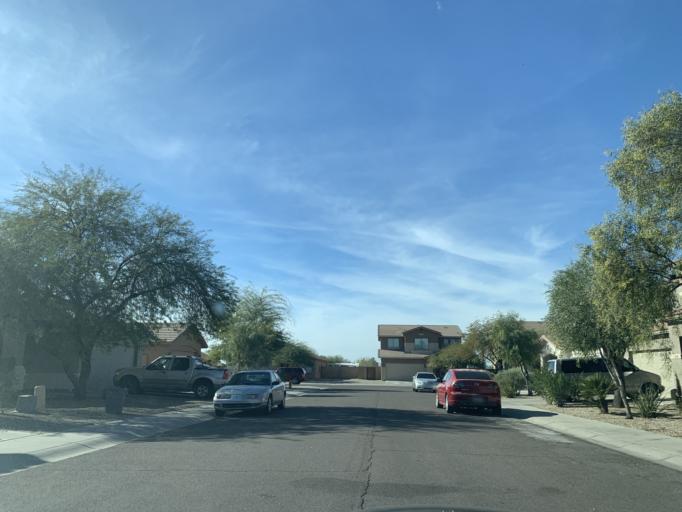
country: US
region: Arizona
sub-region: Maricopa County
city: Laveen
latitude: 33.3889
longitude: -112.1391
